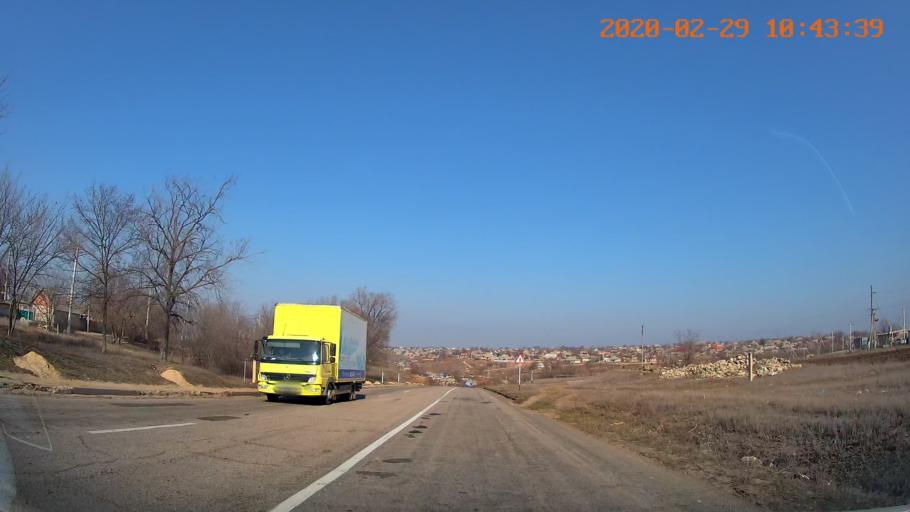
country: MD
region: Telenesti
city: Grigoriopol
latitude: 47.0637
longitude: 29.4024
